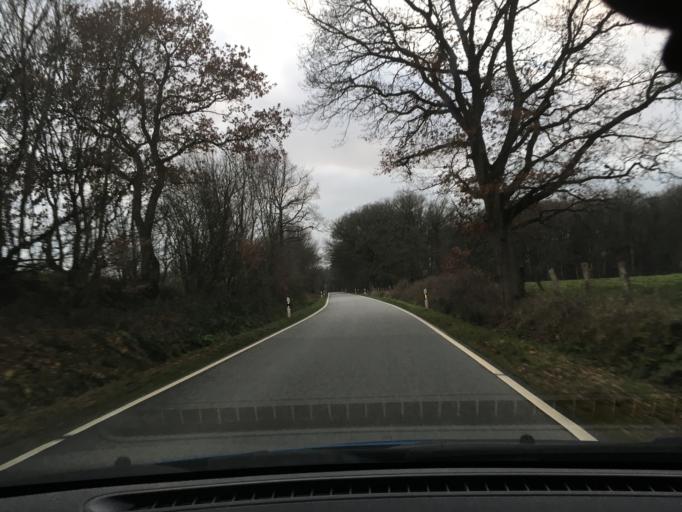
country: DE
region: Schleswig-Holstein
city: Agethorst
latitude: 54.0157
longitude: 9.4370
